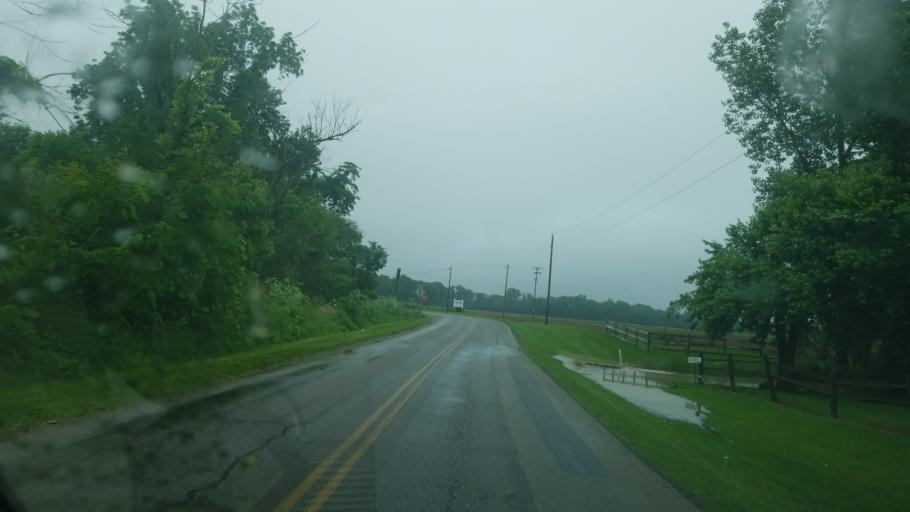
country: US
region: Ohio
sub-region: Morrow County
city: Mount Gilead
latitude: 40.6521
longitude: -82.9109
